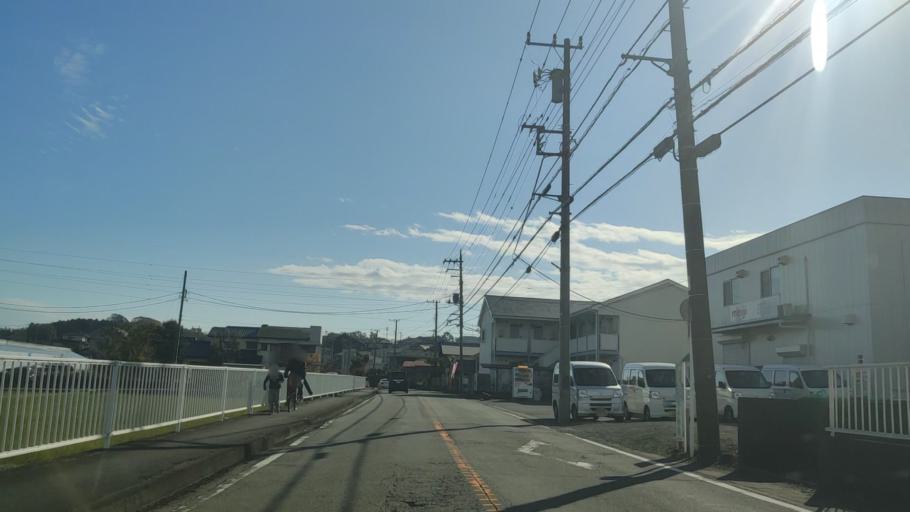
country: JP
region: Kanagawa
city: Atsugi
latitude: 35.4400
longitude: 139.3394
